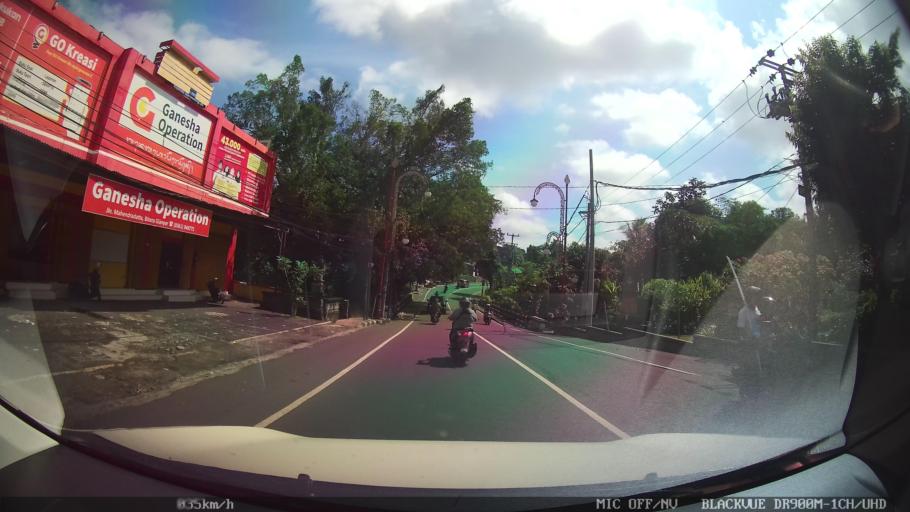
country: ID
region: Bali
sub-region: Kabupaten Gianyar
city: Ubud
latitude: -8.5344
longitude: 115.3108
